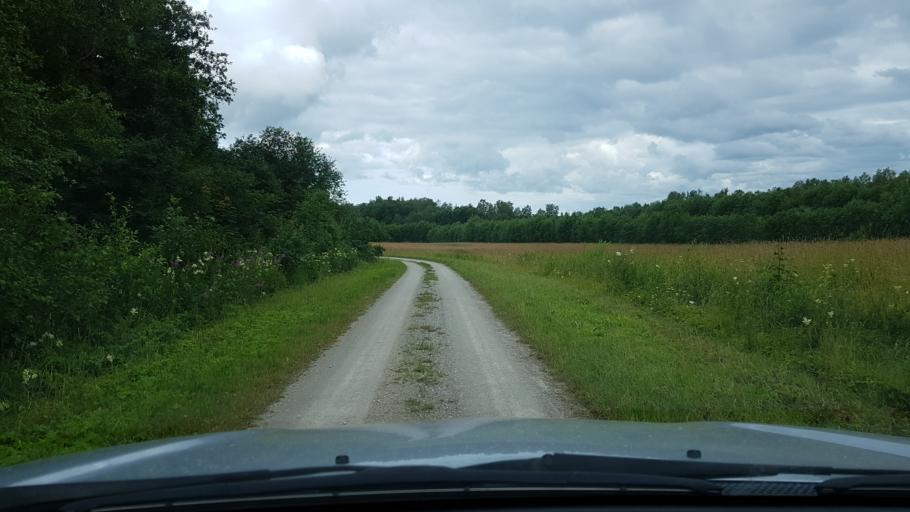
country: EE
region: Ida-Virumaa
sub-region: Narva-Joesuu linn
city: Narva-Joesuu
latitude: 59.4046
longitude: 27.9648
